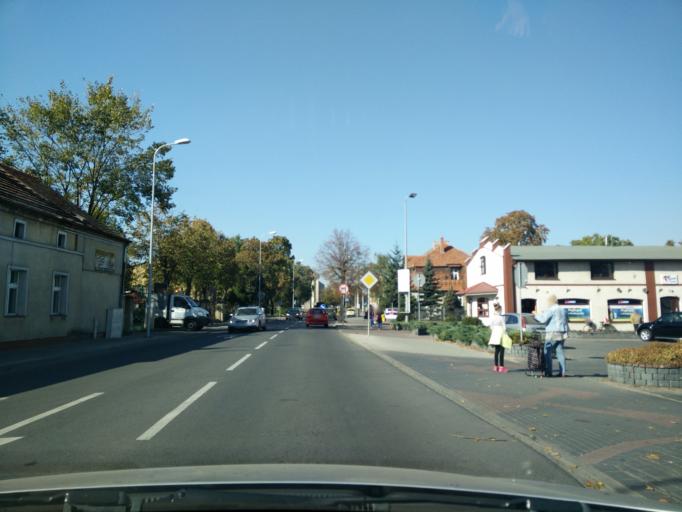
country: PL
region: Greater Poland Voivodeship
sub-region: Powiat sredzki
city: Sroda Wielkopolska
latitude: 52.2303
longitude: 17.2710
